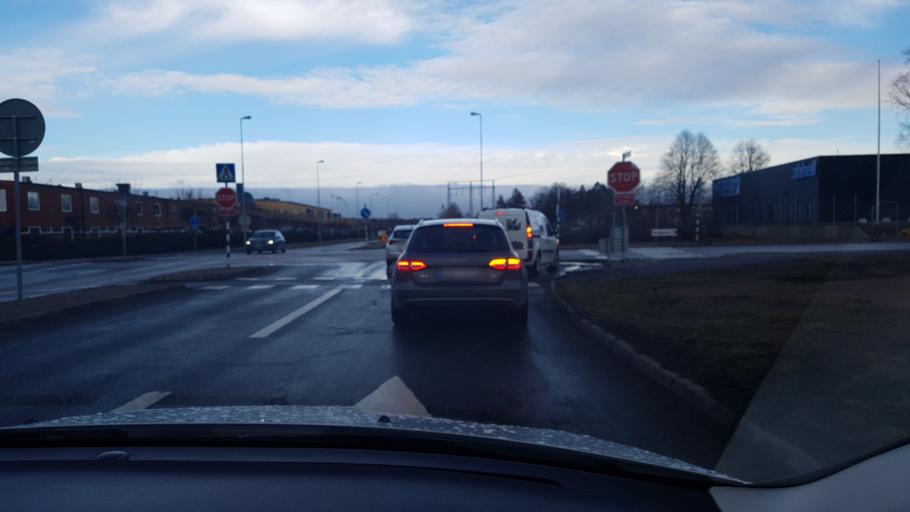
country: SE
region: Skane
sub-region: Hassleholms Kommun
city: Hassleholm
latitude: 56.1620
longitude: 13.7856
